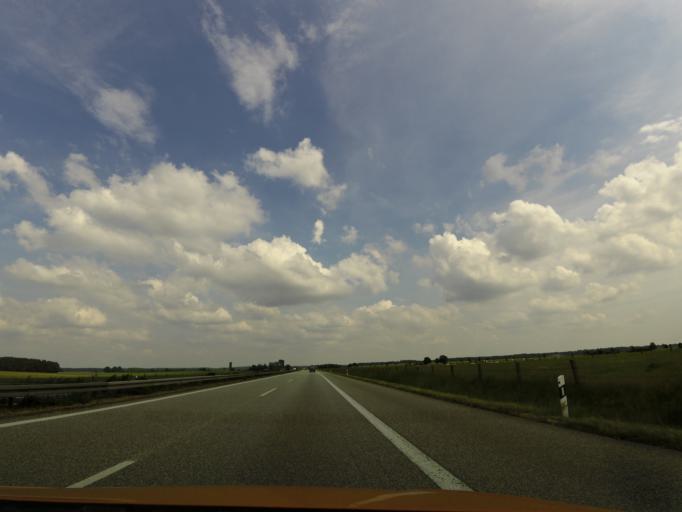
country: DE
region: Mecklenburg-Vorpommern
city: Spornitz
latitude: 53.3686
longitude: 11.6715
